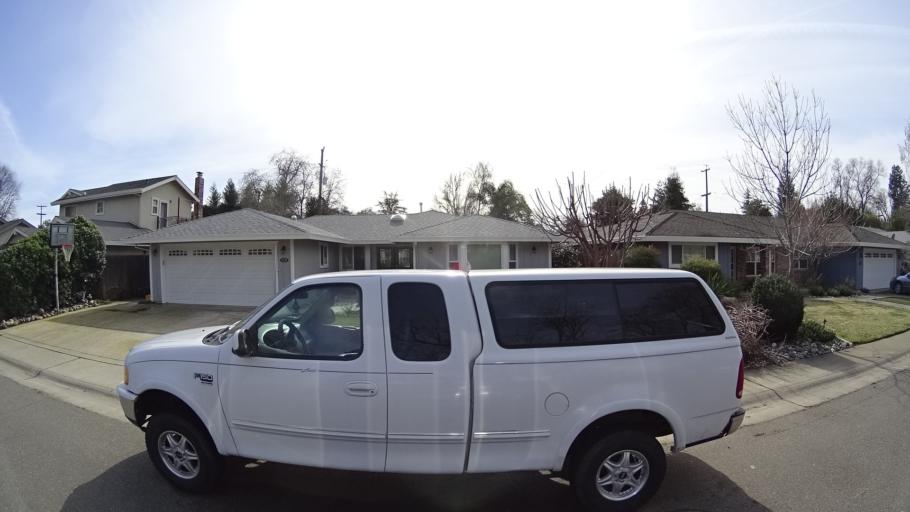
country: US
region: California
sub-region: Yolo County
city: Davis
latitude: 38.5486
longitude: -121.6847
